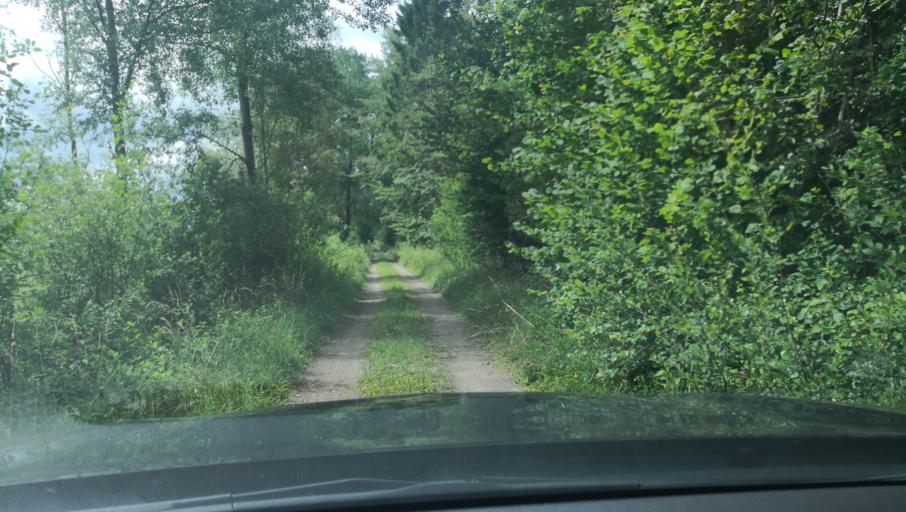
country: SE
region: Skane
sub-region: Simrishamns Kommun
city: Kivik
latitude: 55.6205
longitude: 14.1120
